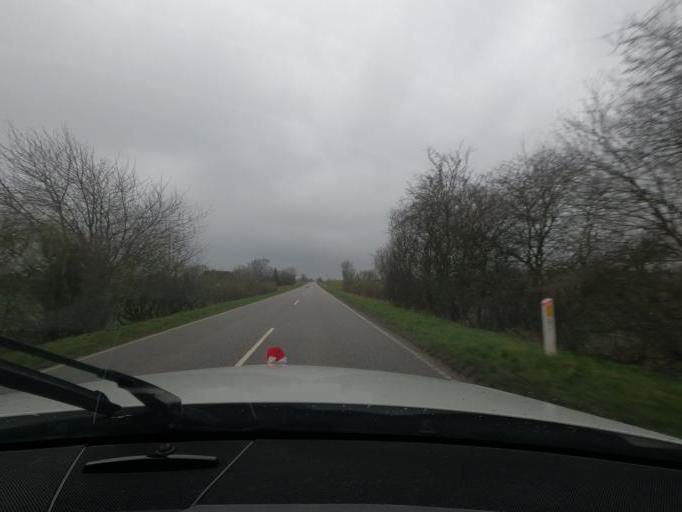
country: DK
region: South Denmark
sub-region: Haderslev Kommune
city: Starup
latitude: 55.2345
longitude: 9.6452
